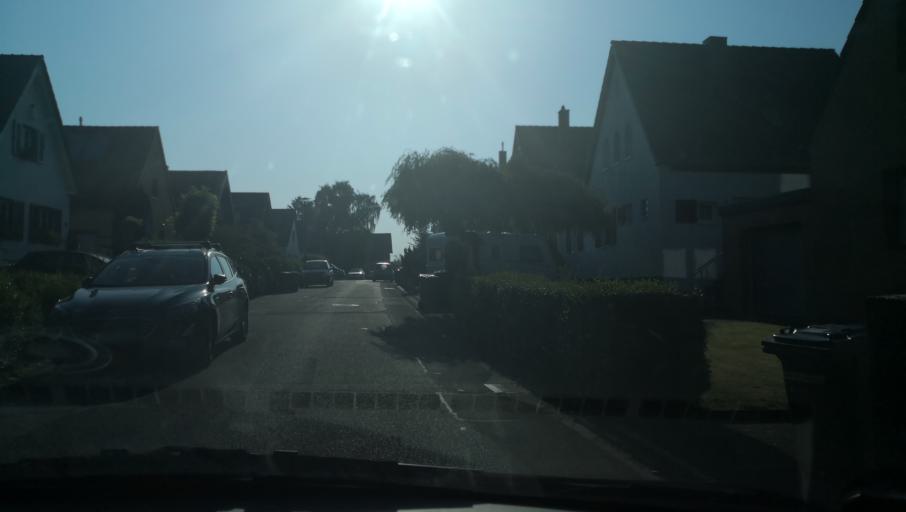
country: DE
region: North Rhine-Westphalia
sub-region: Regierungsbezirk Koln
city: Mengenich
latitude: 50.9538
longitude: 6.8787
